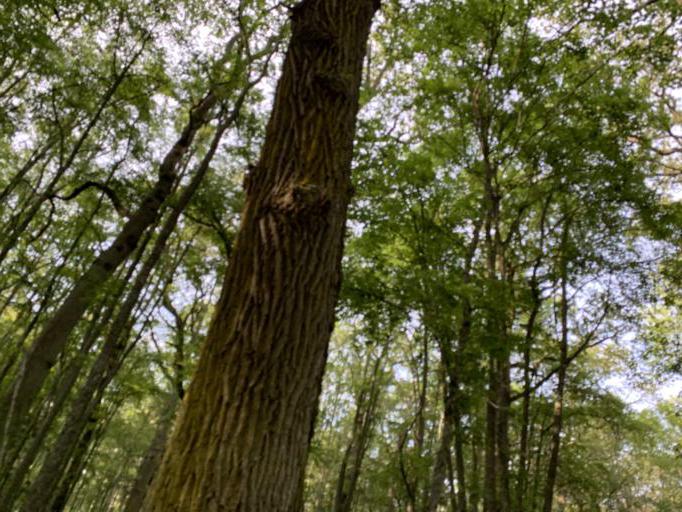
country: SE
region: Vaestmanland
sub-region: Hallstahammars Kommun
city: Kolback
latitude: 59.4692
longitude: 16.2178
